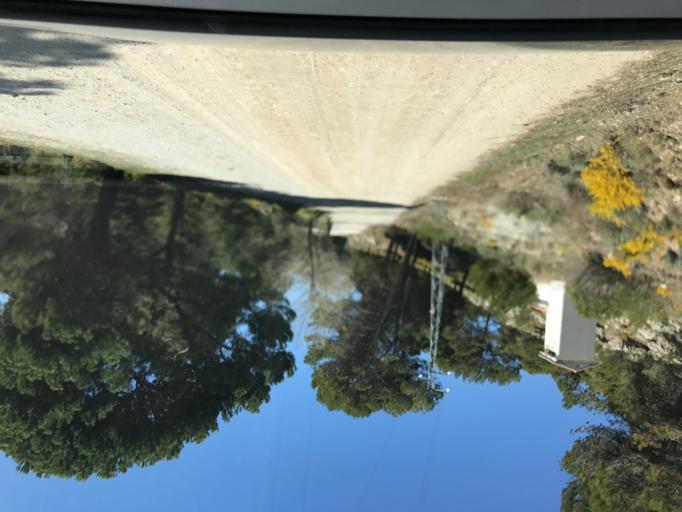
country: ES
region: Andalusia
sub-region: Provincia de Granada
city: Huetor Santillan
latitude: 37.2394
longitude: -3.5302
